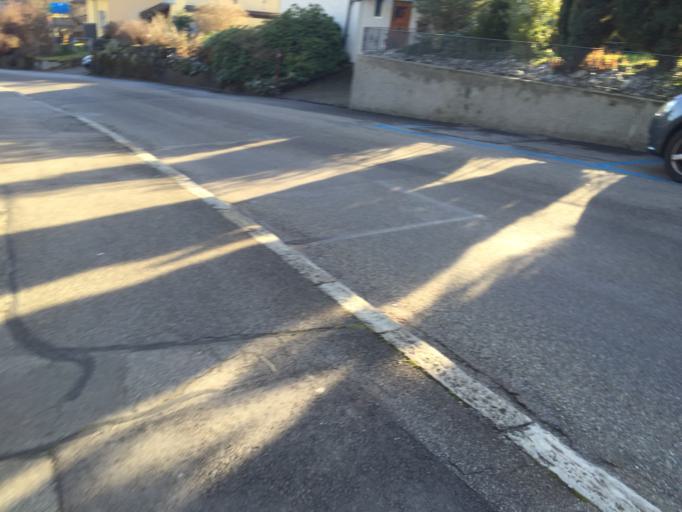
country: CH
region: Bern
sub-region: Bern-Mittelland District
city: Koniz
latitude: 46.9274
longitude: 7.4113
